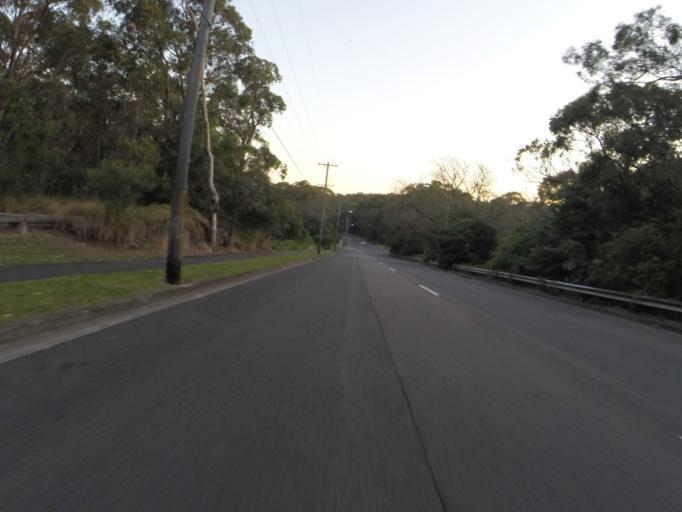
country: AU
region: New South Wales
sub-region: Bankstown
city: Revesby
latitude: -33.9675
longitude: 151.0153
